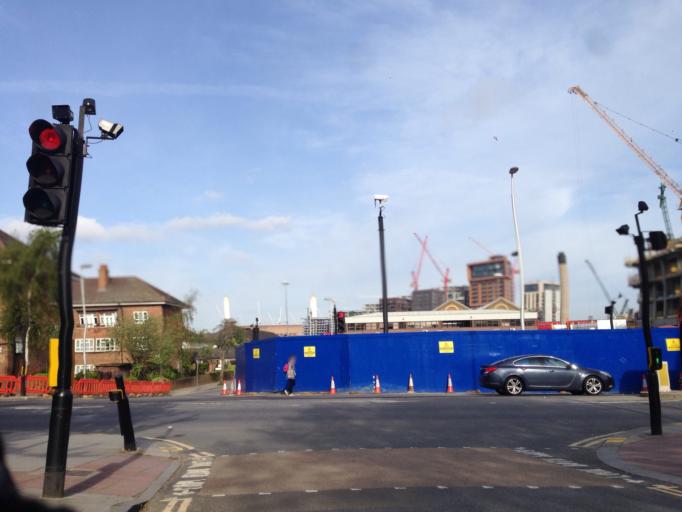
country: GB
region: England
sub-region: Greater London
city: City of Westminster
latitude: 51.4797
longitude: -0.1281
